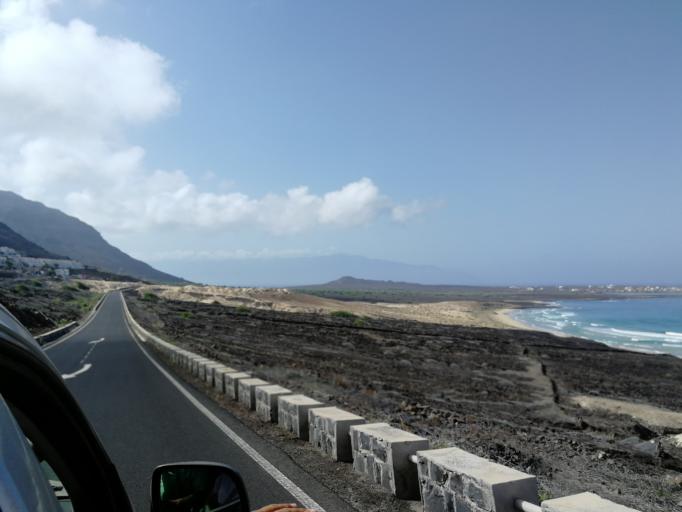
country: CV
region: Sao Vicente
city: Mindelo
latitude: 16.8774
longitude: -24.9124
